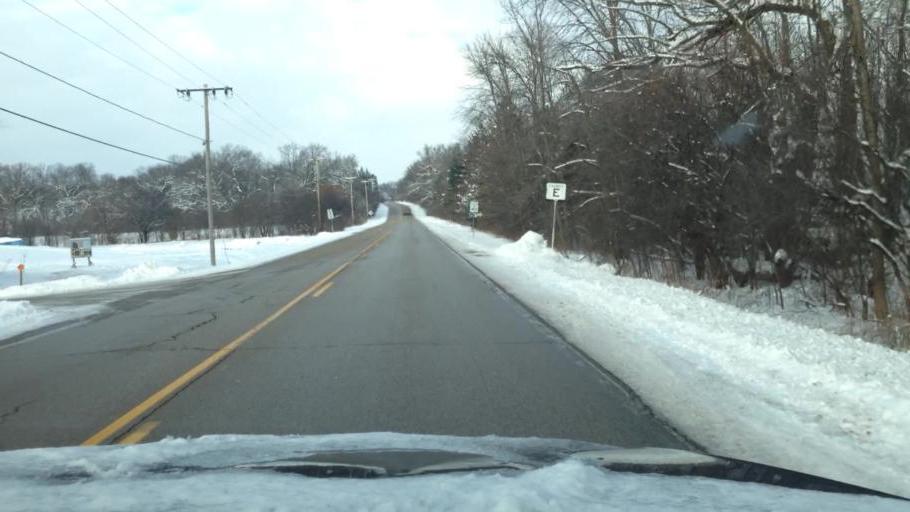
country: US
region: Wisconsin
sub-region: Waukesha County
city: Eagle
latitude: 42.8590
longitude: -88.4312
